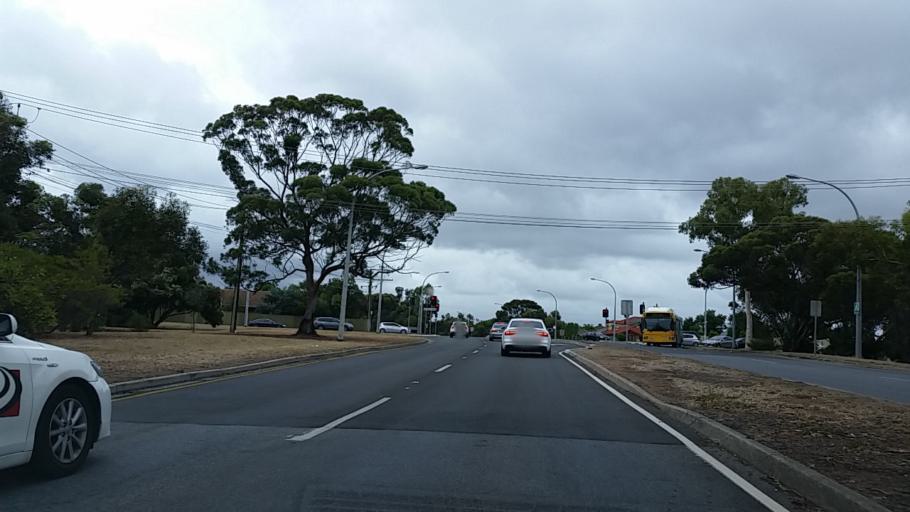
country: AU
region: South Australia
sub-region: Salisbury
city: Ingle Farm
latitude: -34.8349
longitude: 138.6454
